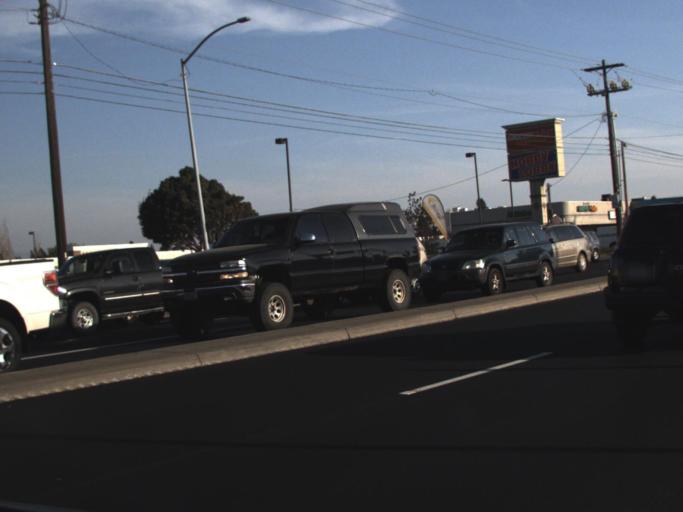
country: US
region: Washington
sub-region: Spokane County
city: Town and Country
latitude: 47.7290
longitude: -117.4115
